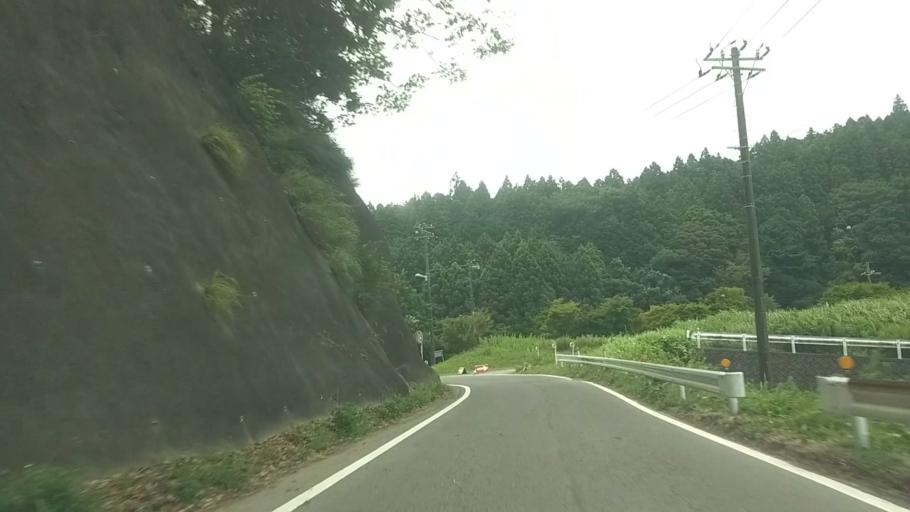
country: JP
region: Chiba
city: Kawaguchi
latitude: 35.2261
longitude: 140.1506
